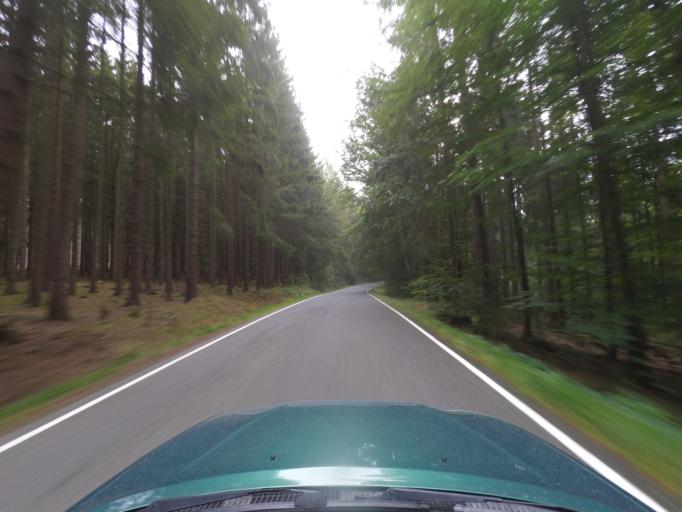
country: CZ
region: Plzensky
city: Bela nad Radbuzou
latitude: 49.5881
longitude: 12.6515
